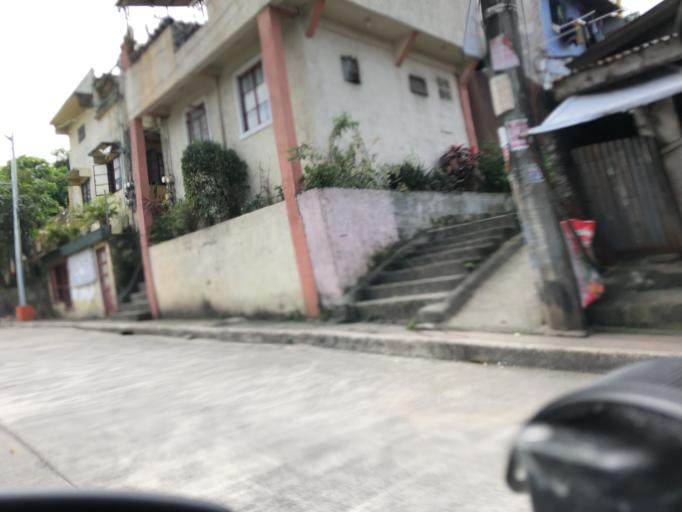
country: PH
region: Central Luzon
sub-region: Province of Bulacan
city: San Jose del Monte
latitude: 14.7480
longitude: 121.0573
